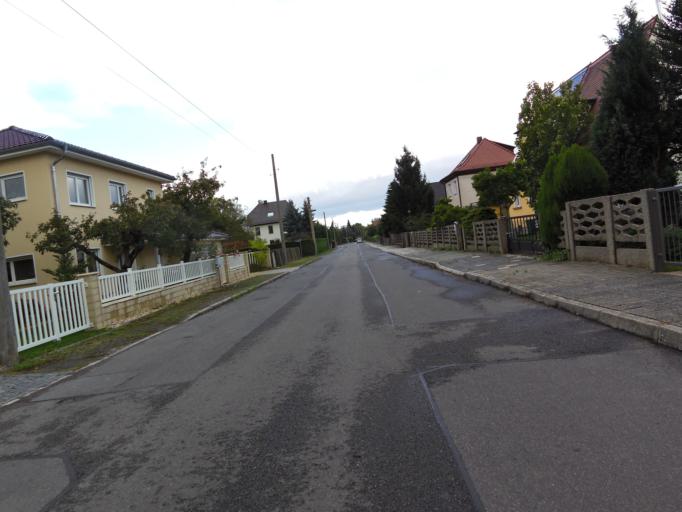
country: DE
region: Saxony
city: Grossposna
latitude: 51.3133
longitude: 12.4687
